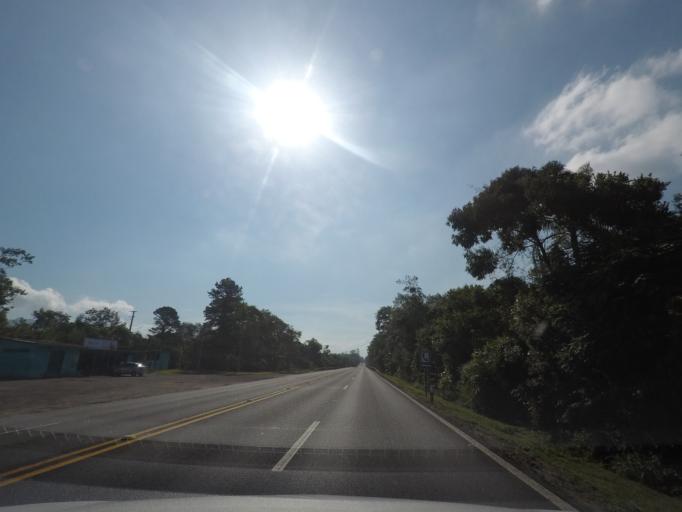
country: BR
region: Parana
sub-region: Pontal Do Parana
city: Pontal do Parana
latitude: -25.6160
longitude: -48.6023
